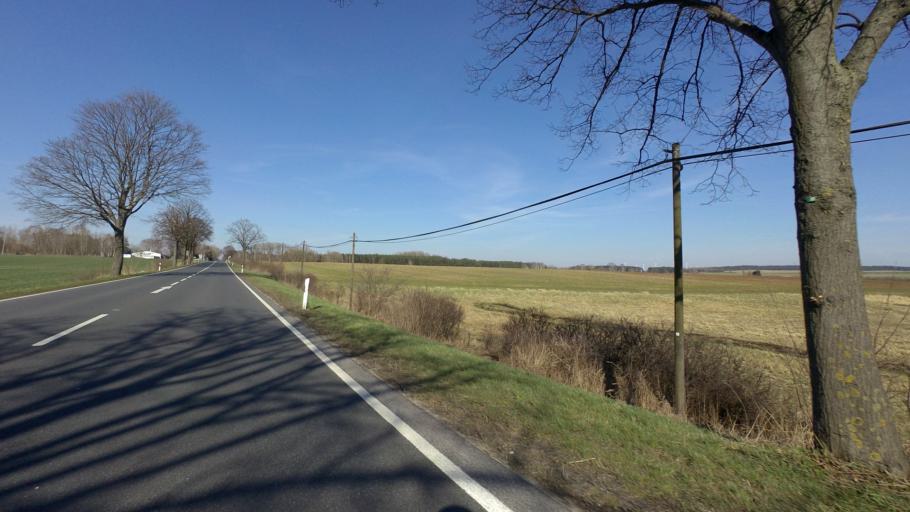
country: DE
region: Brandenburg
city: Angermunde
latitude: 52.9872
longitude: 13.9782
